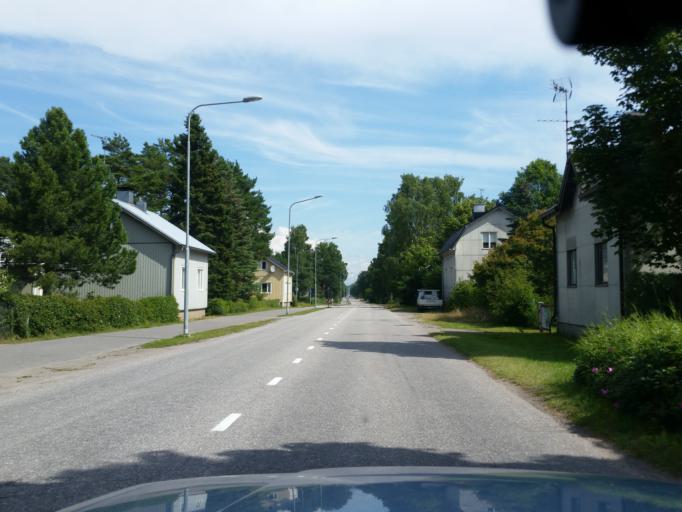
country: FI
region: Uusimaa
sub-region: Raaseporin
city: Hanko
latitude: 59.8340
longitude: 22.9790
